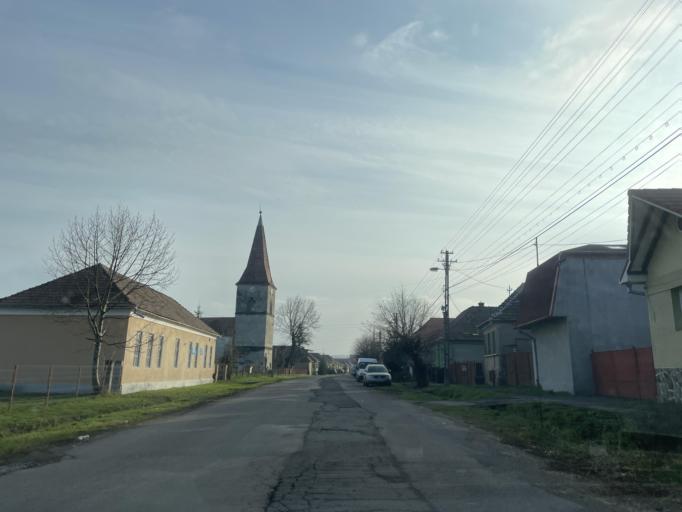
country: RO
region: Mures
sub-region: Municipiul Reghin
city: Apalina
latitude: 46.7504
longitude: 24.6934
